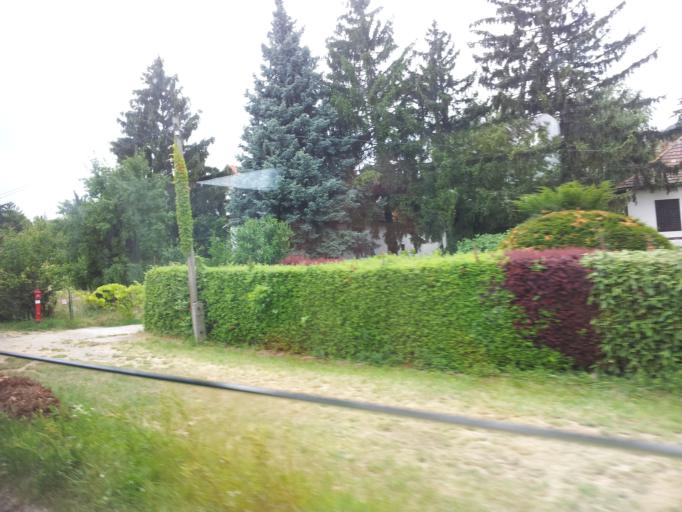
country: HU
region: Veszprem
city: Badacsonytomaj
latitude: 46.7989
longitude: 17.5160
